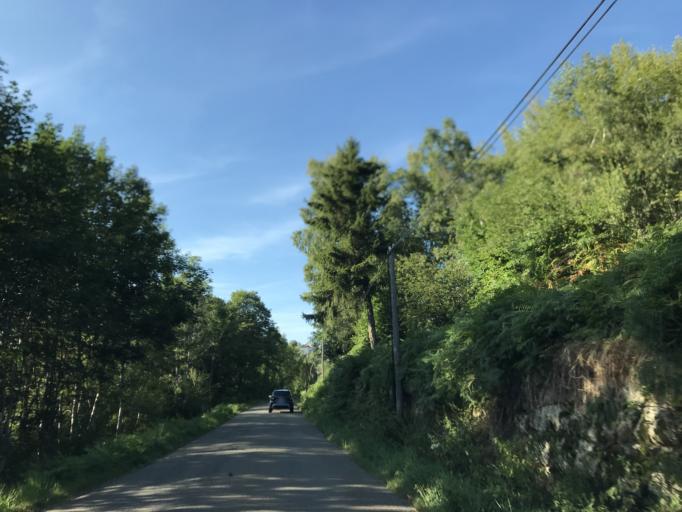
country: FR
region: Auvergne
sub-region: Departement du Puy-de-Dome
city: Job
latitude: 45.7067
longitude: 3.7206
